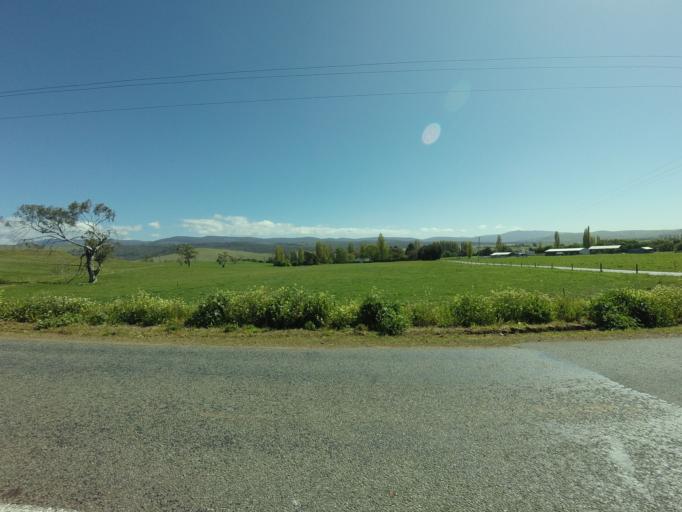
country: AU
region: Tasmania
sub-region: Derwent Valley
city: New Norfolk
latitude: -42.5352
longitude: 146.7529
